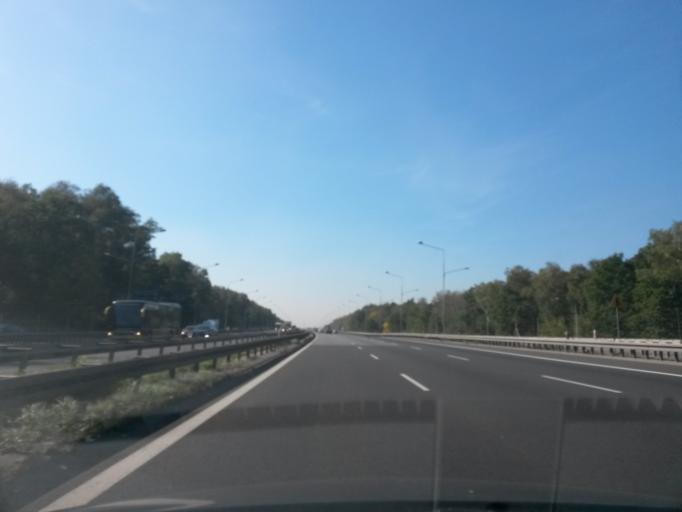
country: PL
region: Silesian Voivodeship
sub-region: Chorzow
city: Chorzow
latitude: 50.2560
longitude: 18.9636
